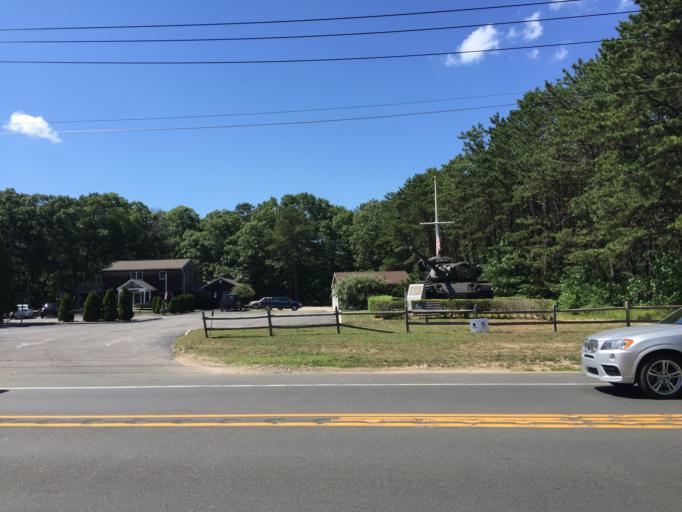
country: US
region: New York
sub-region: Suffolk County
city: East Hampton North
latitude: 40.9517
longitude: -72.2354
